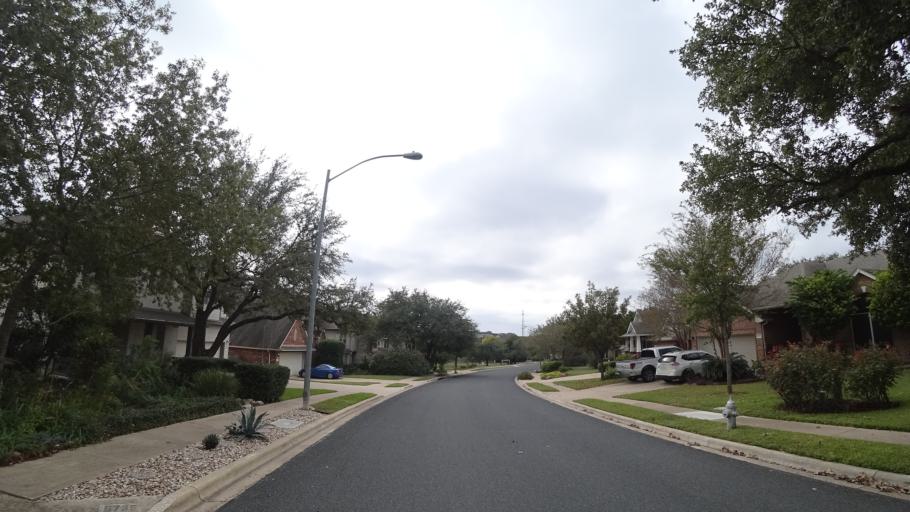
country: US
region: Texas
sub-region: Travis County
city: Barton Creek
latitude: 30.2267
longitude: -97.8764
